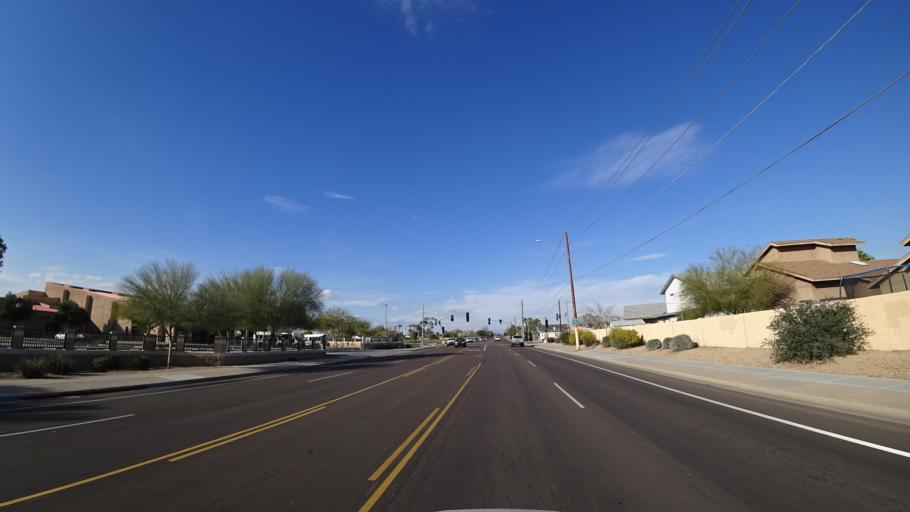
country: US
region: Arizona
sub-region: Maricopa County
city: Peoria
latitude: 33.5873
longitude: -112.2377
